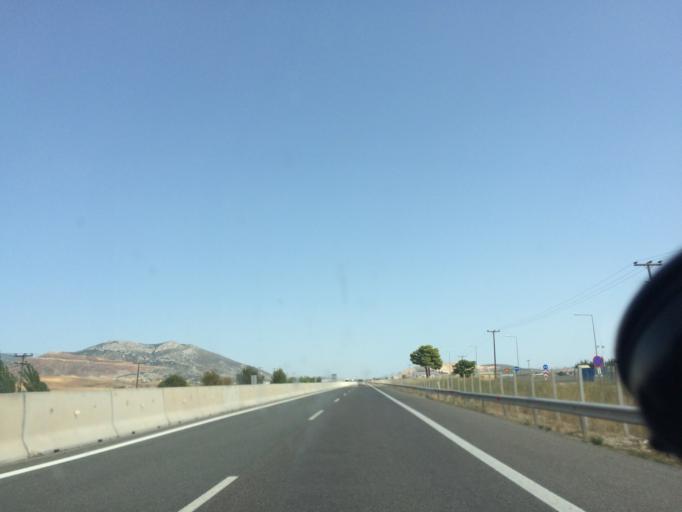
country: GR
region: Central Greece
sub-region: Nomos Voiotias
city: Thivai
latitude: 38.3660
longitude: 23.3336
